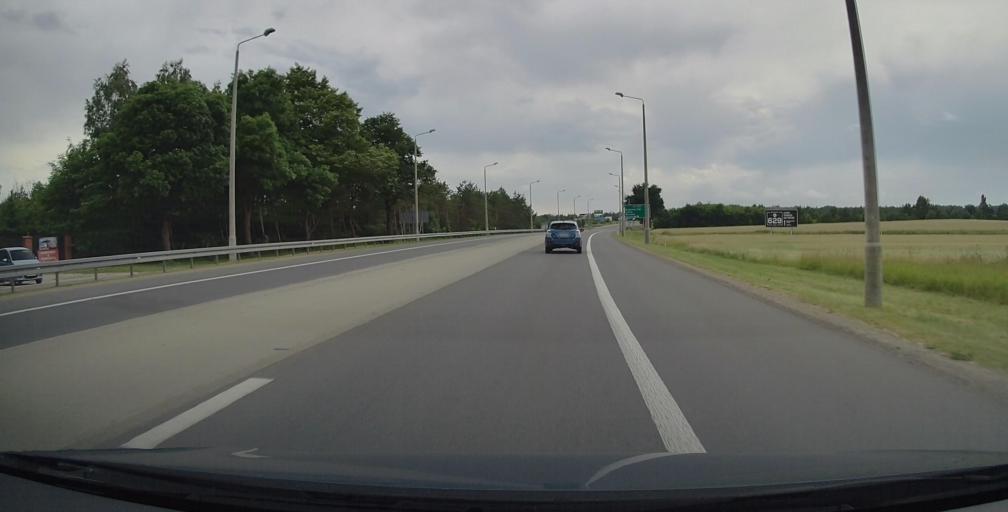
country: PL
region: Lublin Voivodeship
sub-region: Biala Podlaska
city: Biala Podlaska
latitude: 52.0338
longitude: 23.0642
